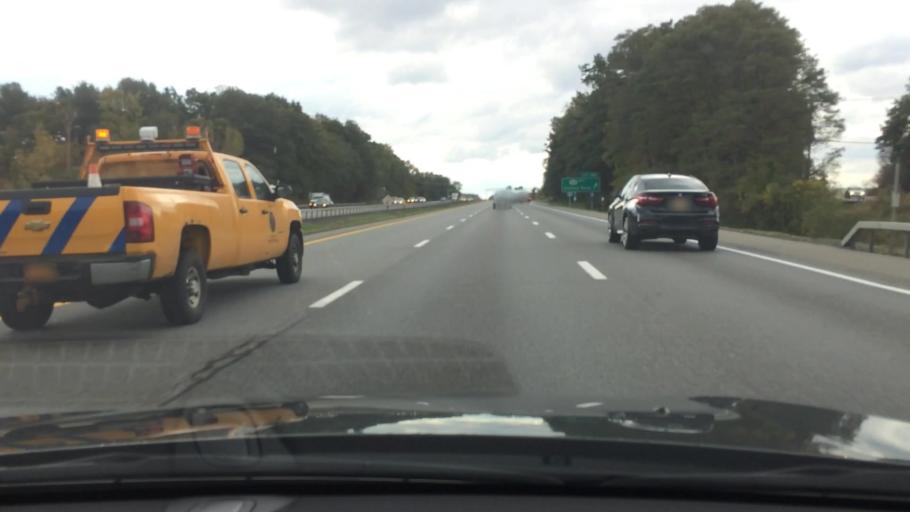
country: US
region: New York
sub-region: Saratoga County
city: Country Knolls
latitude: 42.8690
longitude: -73.7766
